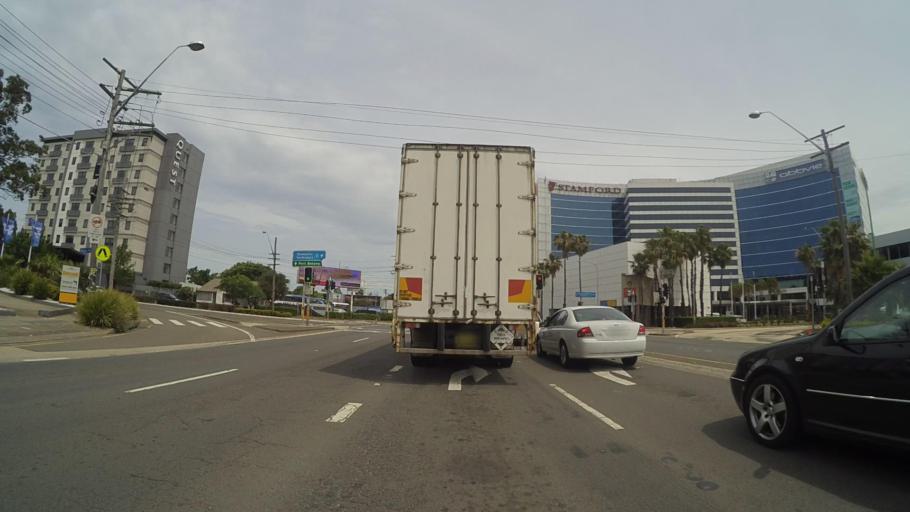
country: AU
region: New South Wales
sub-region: Botany Bay
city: Mascot
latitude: -33.9303
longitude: 151.1867
